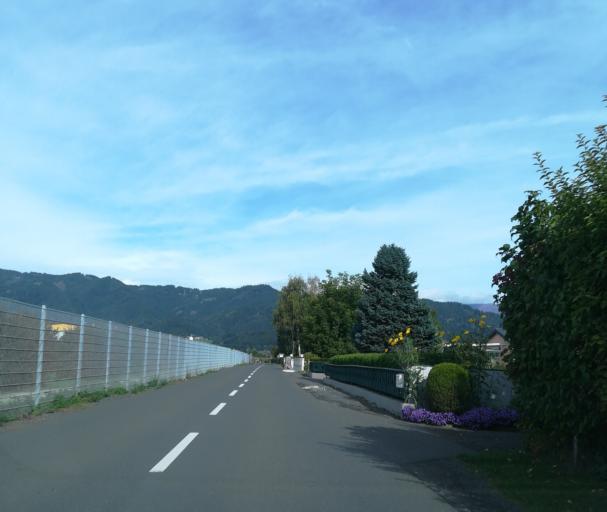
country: AT
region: Styria
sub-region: Politischer Bezirk Murtal
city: Zeltweg
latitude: 47.2000
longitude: 14.7637
